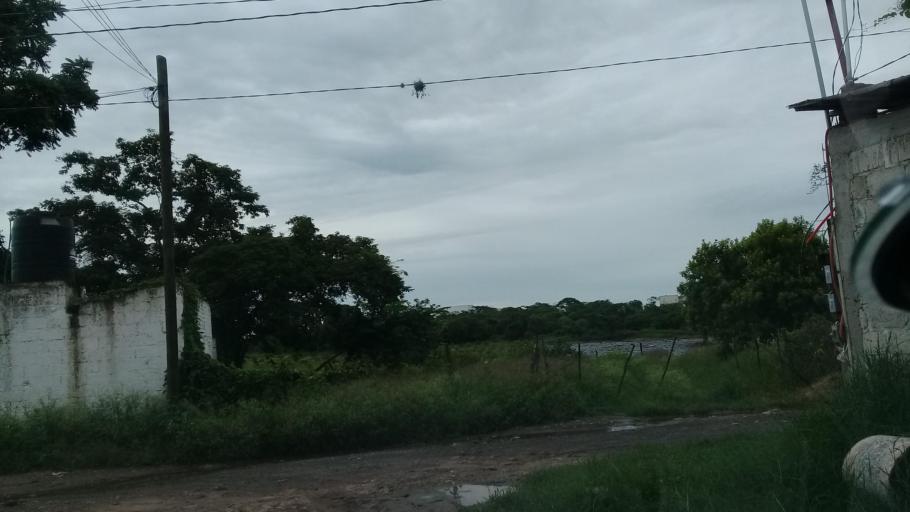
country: MX
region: Veracruz
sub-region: Emiliano Zapata
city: Dos Rios
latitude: 19.4788
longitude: -96.7984
